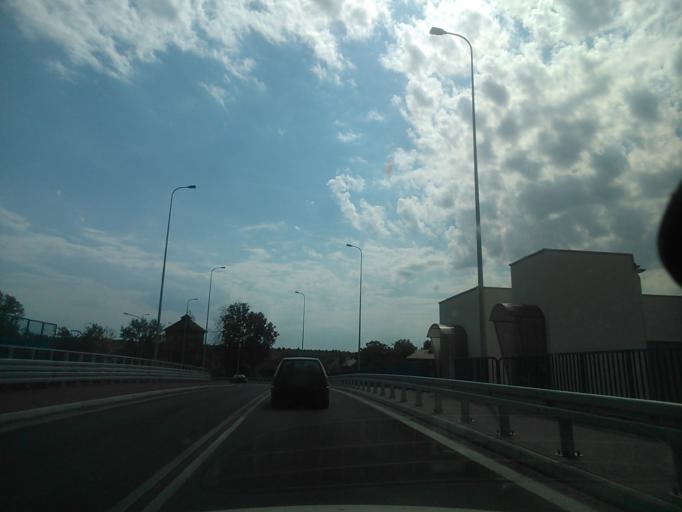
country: PL
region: Warmian-Masurian Voivodeship
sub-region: Powiat dzialdowski
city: Ilowo -Osada
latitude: 53.1662
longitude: 20.2928
